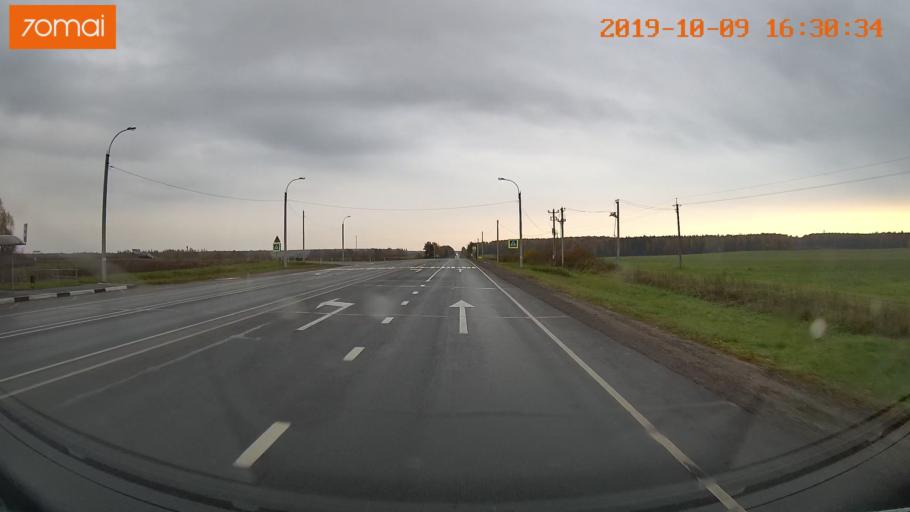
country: RU
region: Kostroma
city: Oktyabr'skiy
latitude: 57.6177
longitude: 40.9415
